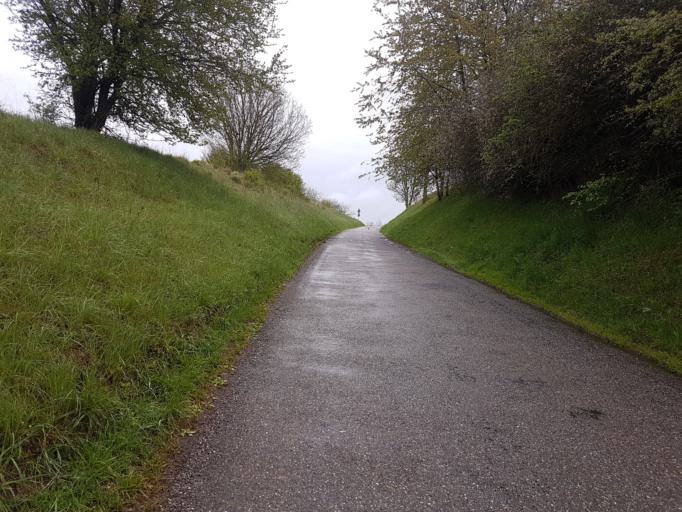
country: DE
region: Baden-Wuerttemberg
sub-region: Freiburg Region
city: Rottweil
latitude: 48.1912
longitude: 8.6166
